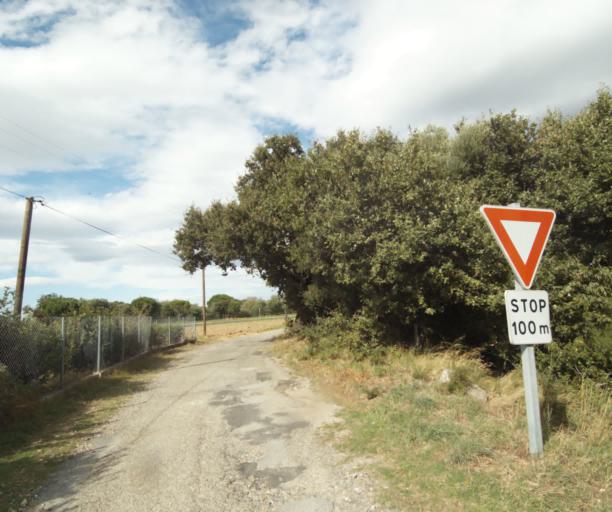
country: FR
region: Languedoc-Roussillon
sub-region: Departement des Pyrenees-Orientales
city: Sant Andreu de Sureda
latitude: 42.5314
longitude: 2.9863
